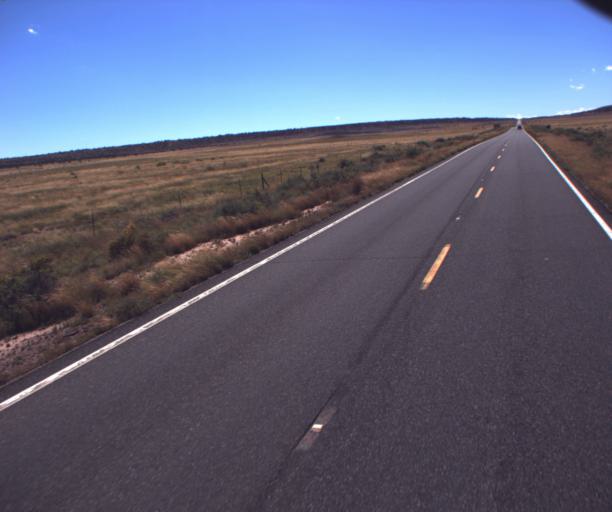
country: US
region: Arizona
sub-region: Apache County
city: Saint Johns
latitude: 34.6795
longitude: -109.2831
